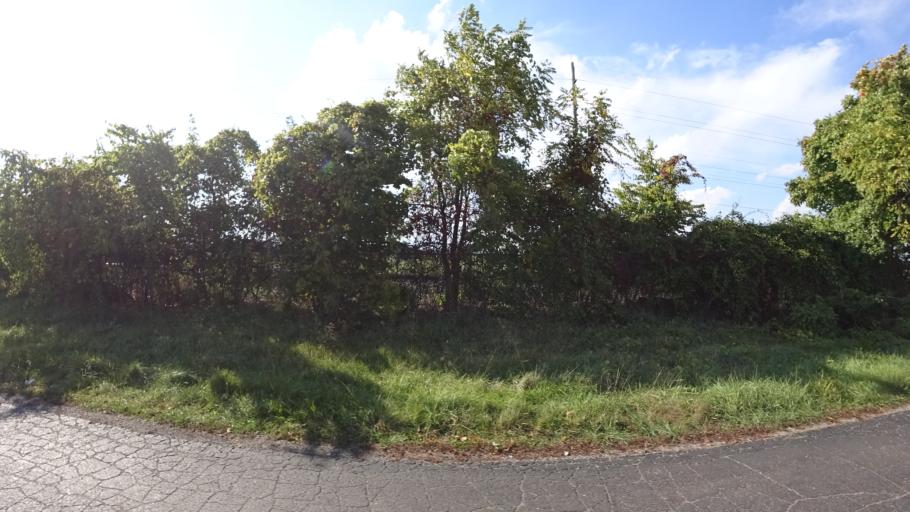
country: US
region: Michigan
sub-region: Saint Joseph County
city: Three Rivers
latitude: 41.9634
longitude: -85.6364
